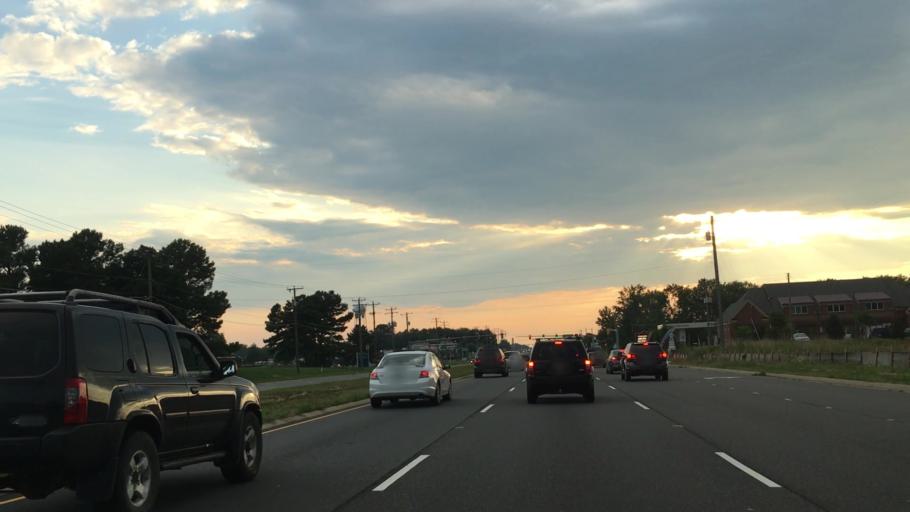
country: US
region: Virginia
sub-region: Stafford County
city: Falmouth
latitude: 38.2895
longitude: -77.5441
